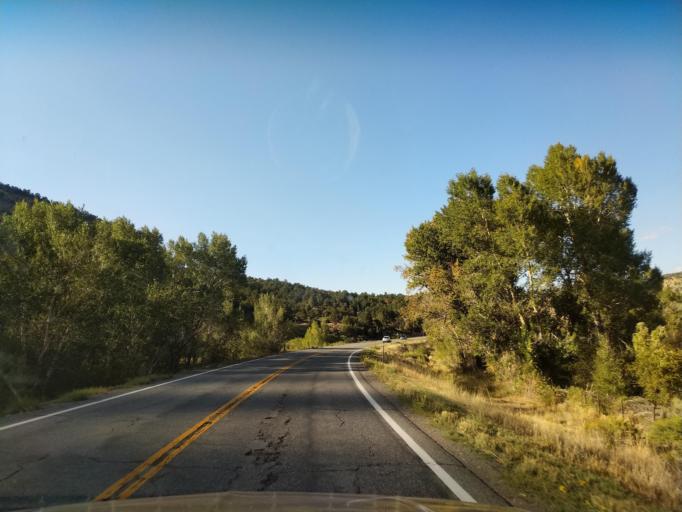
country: US
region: Colorado
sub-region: Montrose County
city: Montrose
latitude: 38.2735
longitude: -107.7659
